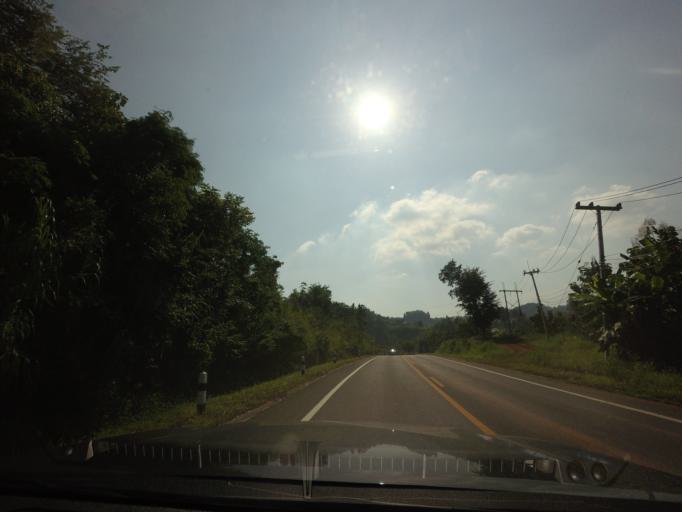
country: TH
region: Nan
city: Santi Suk
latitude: 18.9197
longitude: 100.8899
